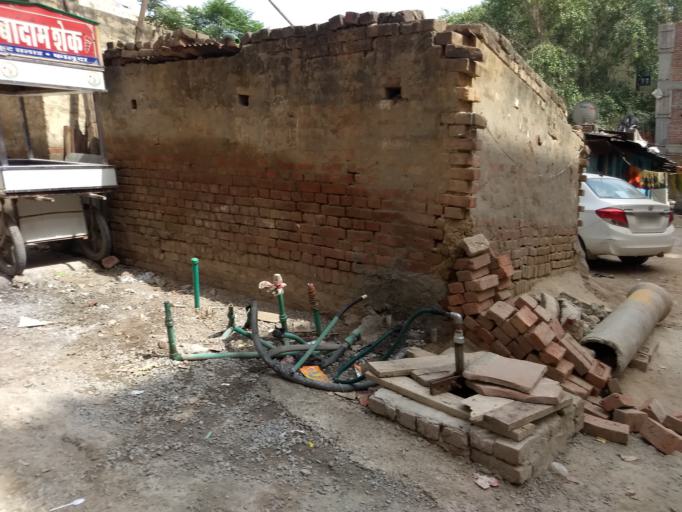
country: IN
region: NCT
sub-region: Central Delhi
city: Karol Bagh
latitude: 28.5410
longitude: 77.1255
